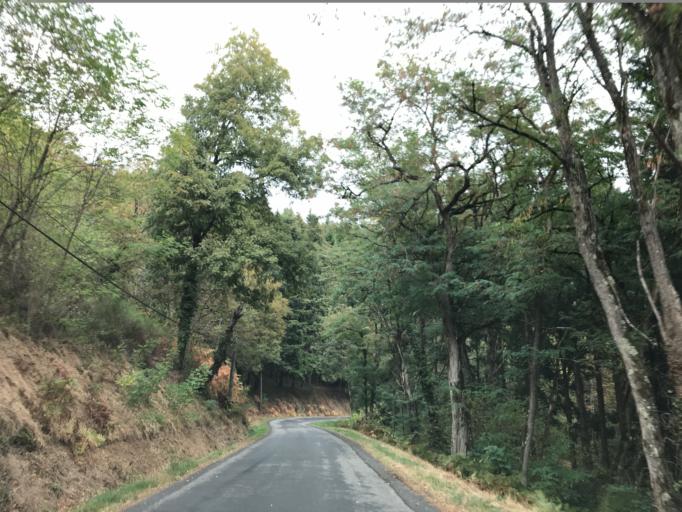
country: FR
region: Auvergne
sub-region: Departement du Puy-de-Dome
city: Escoutoux
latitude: 45.8348
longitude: 3.5721
